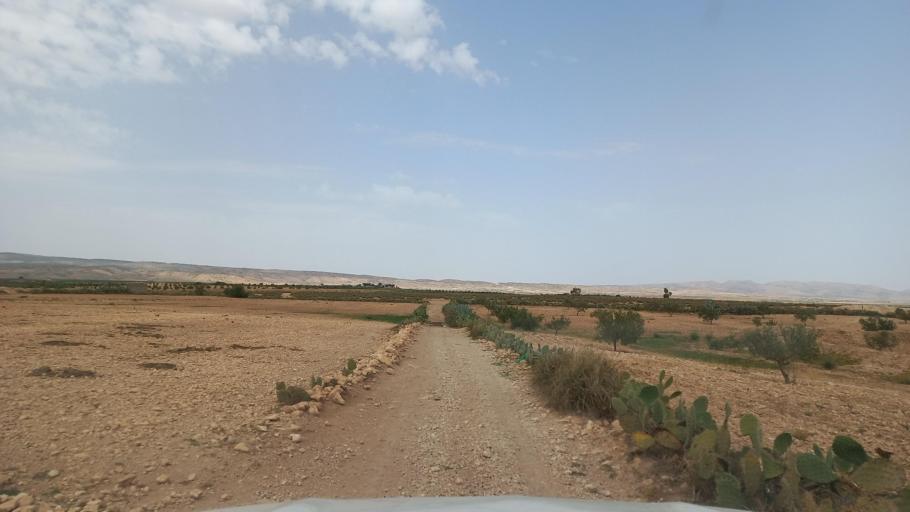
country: TN
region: Al Qasrayn
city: Kasserine
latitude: 35.2909
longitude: 9.0056
